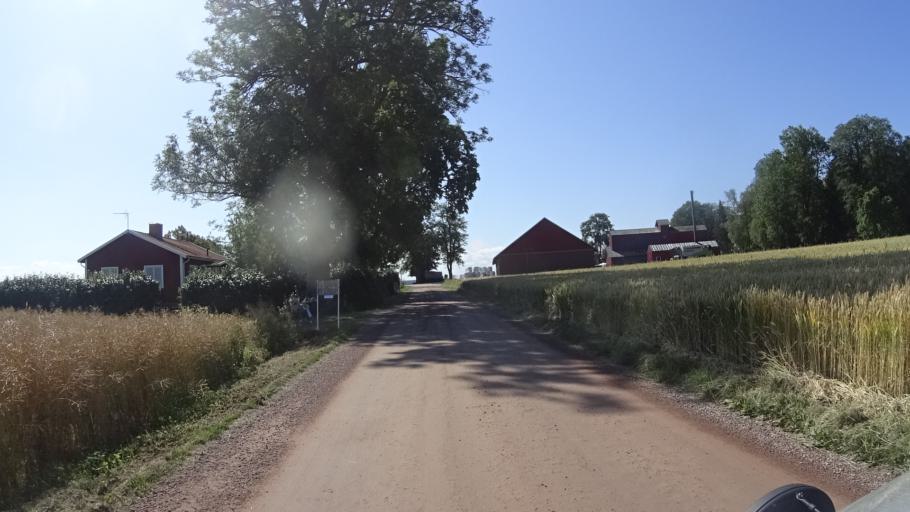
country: SE
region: OEstergoetland
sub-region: Vadstena Kommun
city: Herrestad
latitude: 58.3248
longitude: 14.8260
